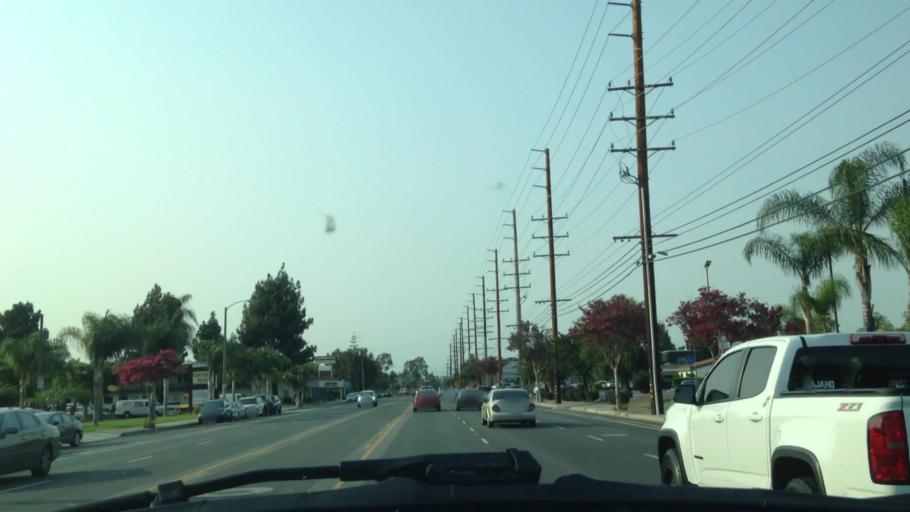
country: US
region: California
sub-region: Orange County
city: Orange
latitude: 33.7692
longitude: -117.8518
